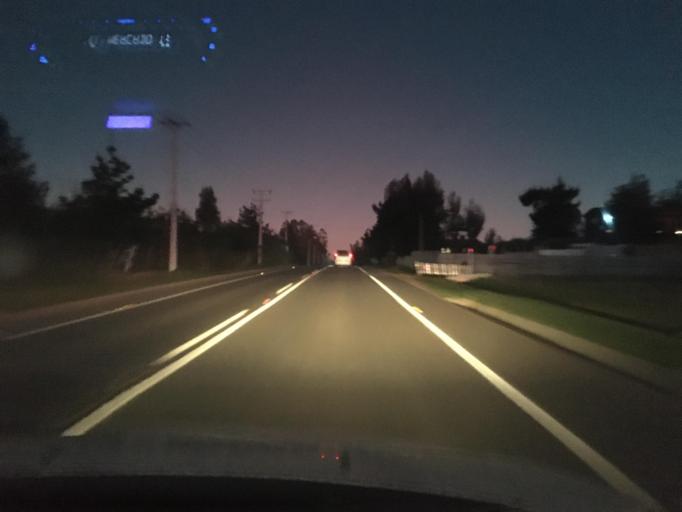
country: CL
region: Valparaiso
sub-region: San Antonio Province
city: El Tabo
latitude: -33.4278
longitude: -71.6568
